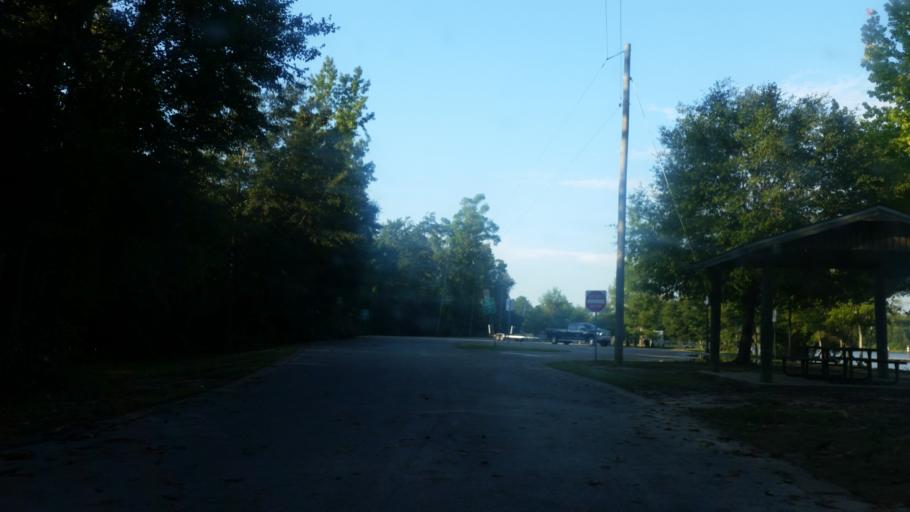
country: US
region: Florida
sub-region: Santa Rosa County
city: Milton
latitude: 30.6279
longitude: -87.0324
